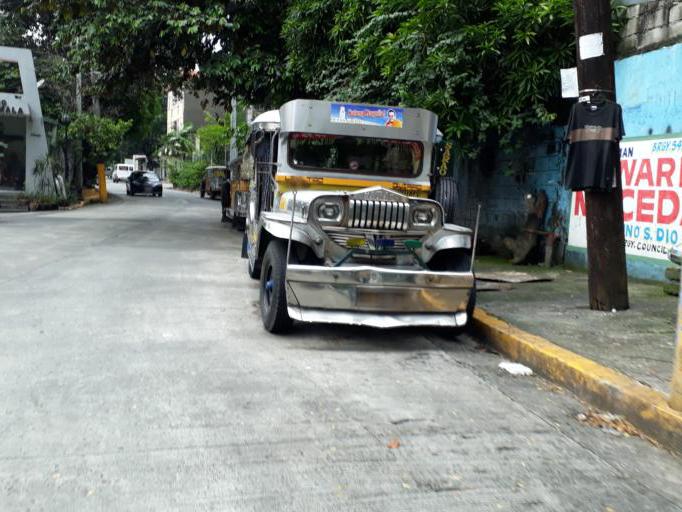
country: PH
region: Metro Manila
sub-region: City of Manila
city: Manila
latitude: 14.6106
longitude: 121.0003
